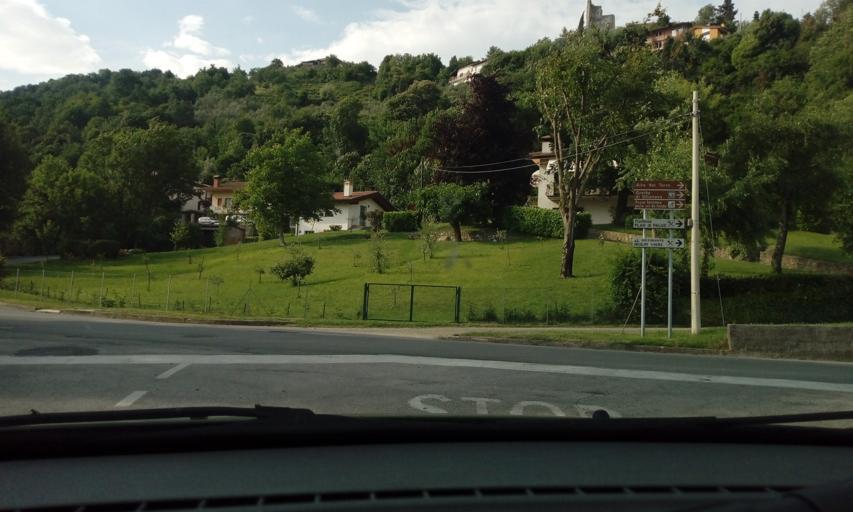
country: IT
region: Friuli Venezia Giulia
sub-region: Provincia di Udine
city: Tarcento
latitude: 46.2163
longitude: 13.2131
